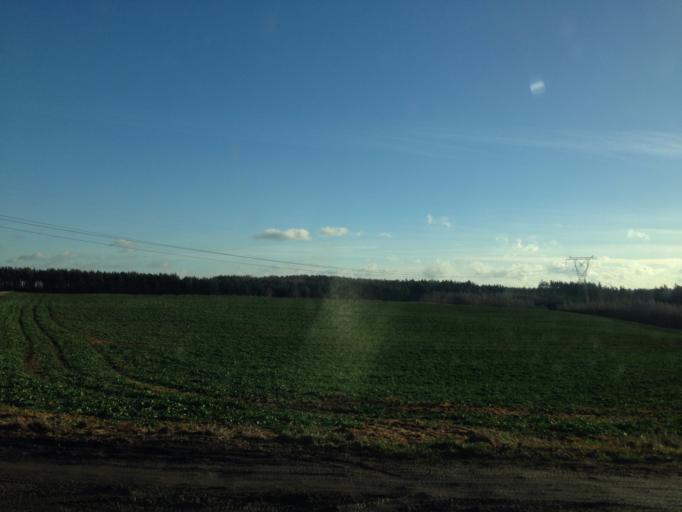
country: PL
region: Pomeranian Voivodeship
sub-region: Powiat kwidzynski
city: Gardeja
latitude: 53.6271
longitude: 19.0268
